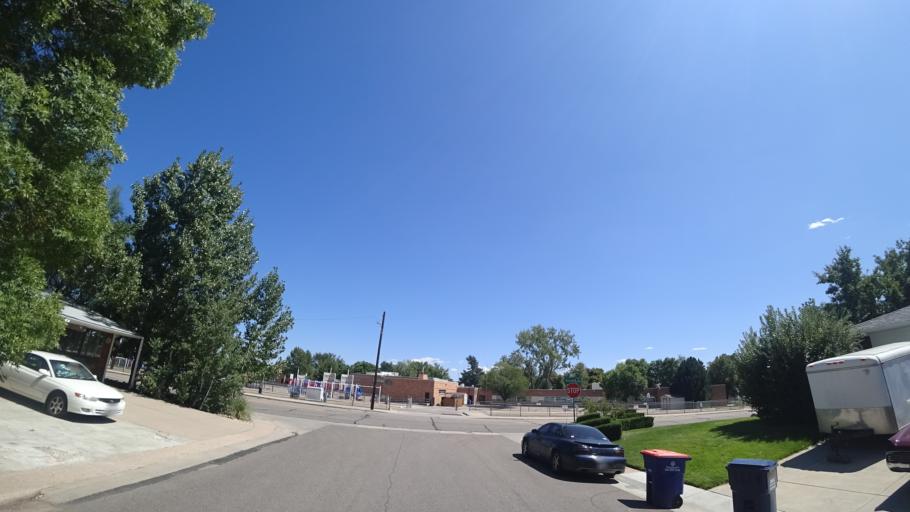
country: US
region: Colorado
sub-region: Arapahoe County
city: Littleton
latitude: 39.6094
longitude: -104.9919
